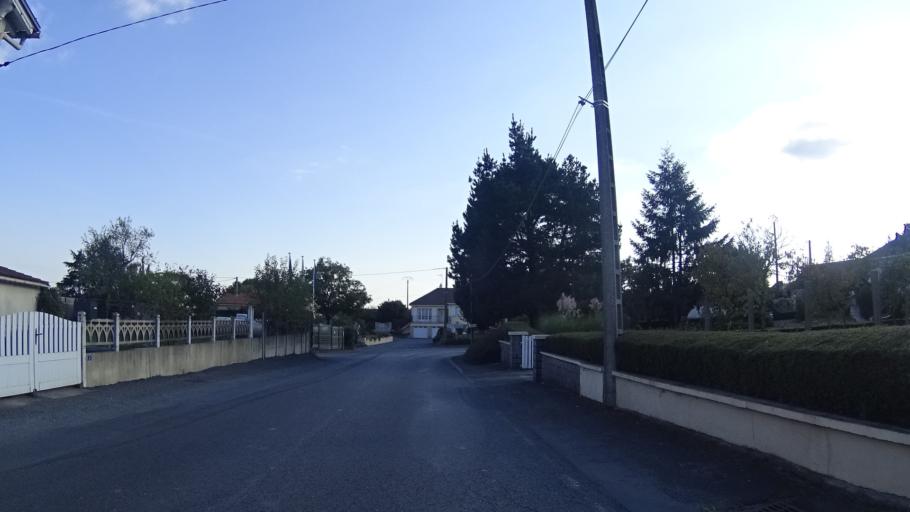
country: FR
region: Pays de la Loire
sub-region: Departement de Maine-et-Loire
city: Saint-Florent-le-Vieil
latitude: 47.3611
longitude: -1.0064
